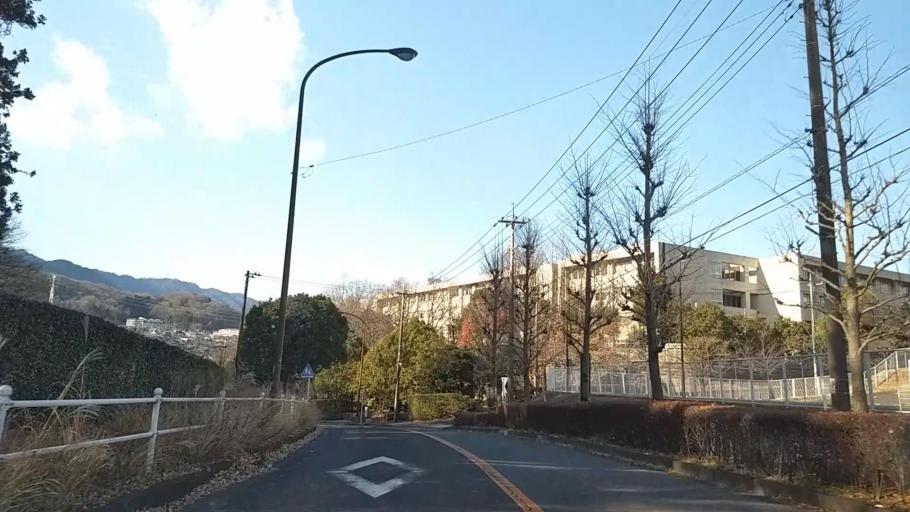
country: JP
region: Kanagawa
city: Atsugi
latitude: 35.4473
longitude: 139.3134
